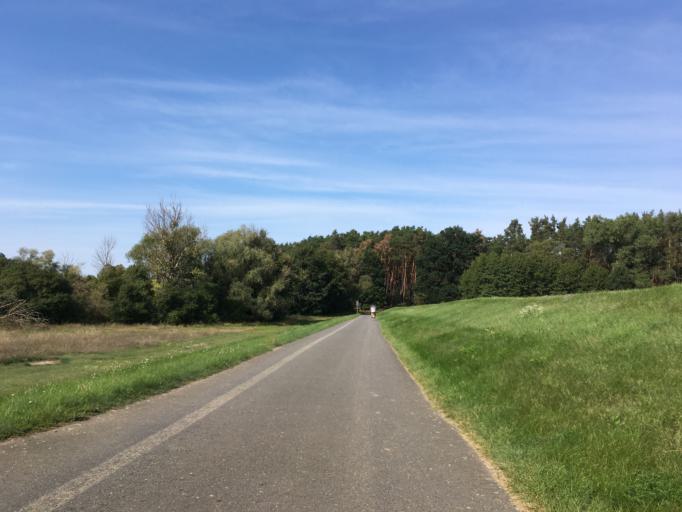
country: DE
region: Brandenburg
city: Neuzelle
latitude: 52.0569
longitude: 14.7425
